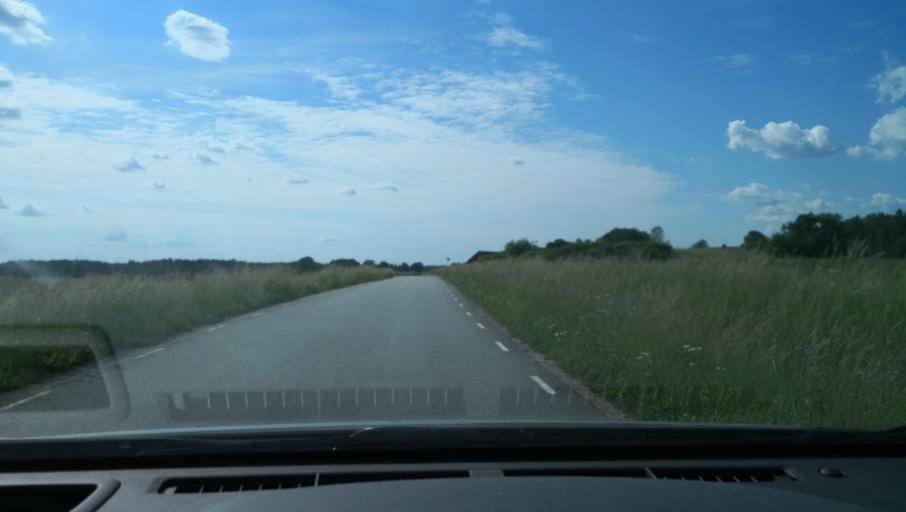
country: SE
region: Uppsala
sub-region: Enkopings Kommun
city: Orsundsbro
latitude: 59.8157
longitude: 17.3403
